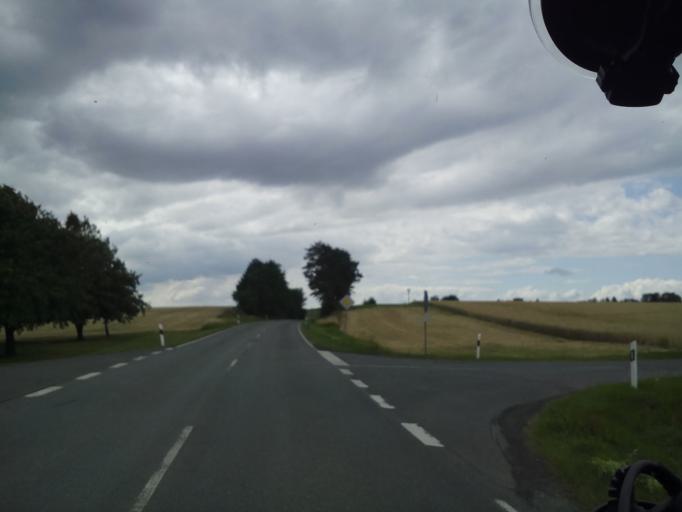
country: DE
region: Bavaria
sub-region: Upper Franconia
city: Sonnefeld
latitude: 50.2493
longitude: 11.0870
